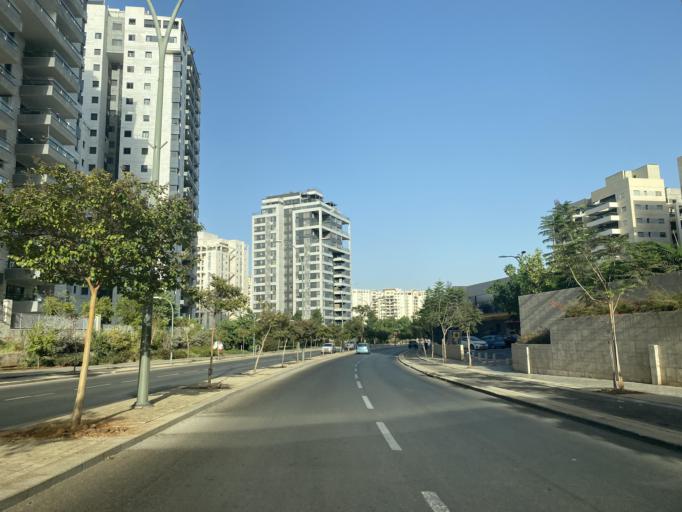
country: IL
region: Central District
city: Kfar Saba
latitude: 32.1646
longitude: 34.9036
